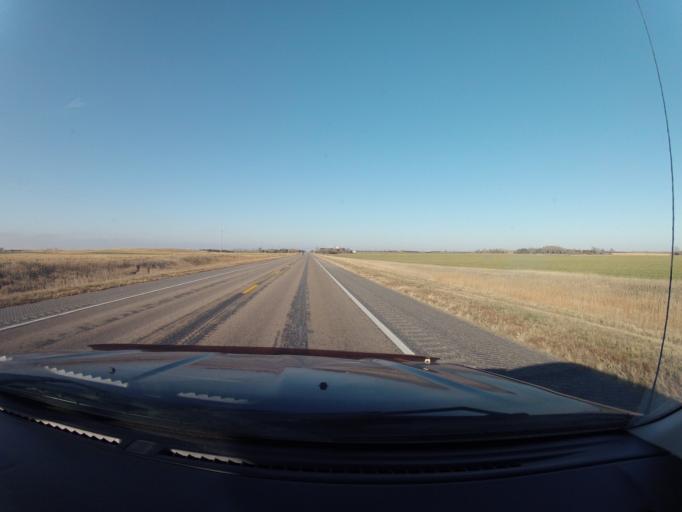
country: US
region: Nebraska
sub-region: Kearney County
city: Minden
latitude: 40.5871
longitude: -98.9517
